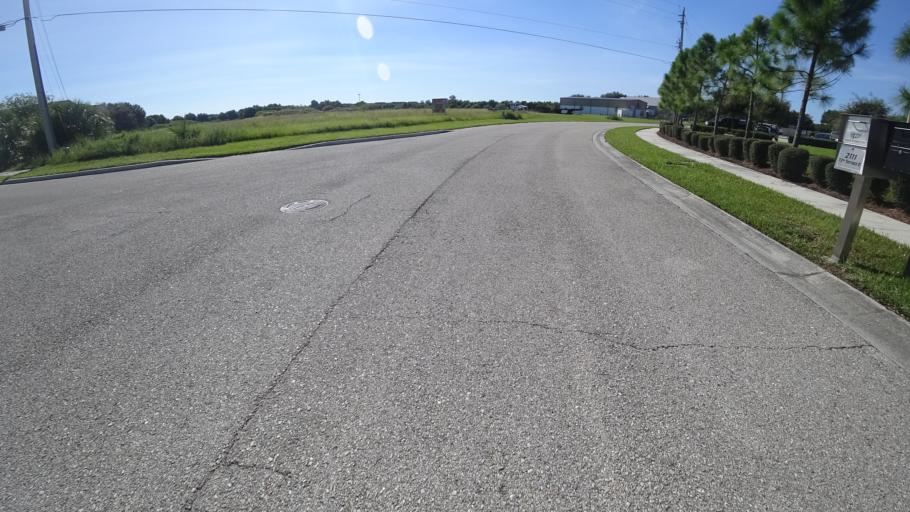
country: US
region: Florida
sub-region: Manatee County
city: Whitfield
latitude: 27.4107
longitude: -82.5377
